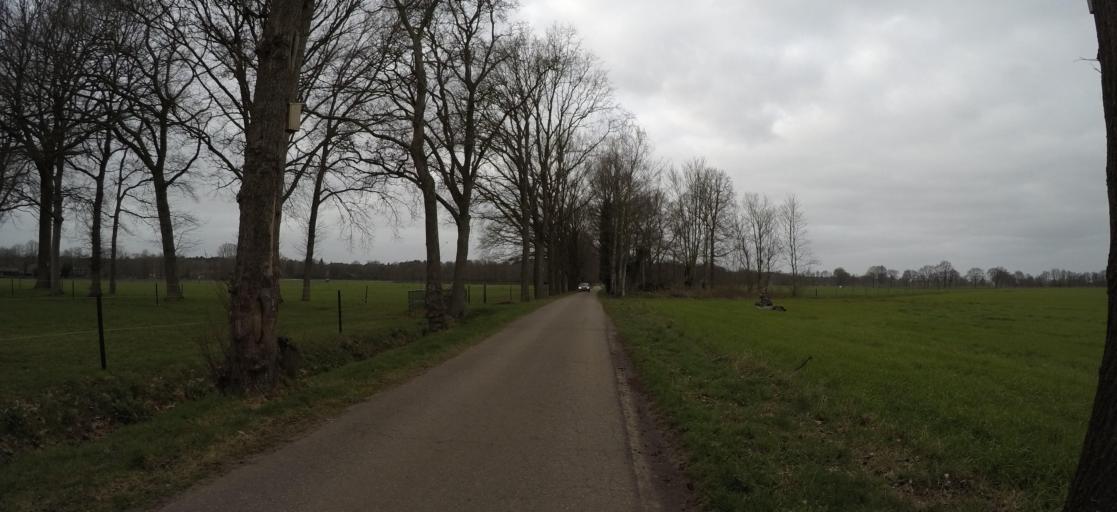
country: NL
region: North Brabant
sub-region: Gemeente Woensdrecht
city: Woensdrecht
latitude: 51.4236
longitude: 4.3909
